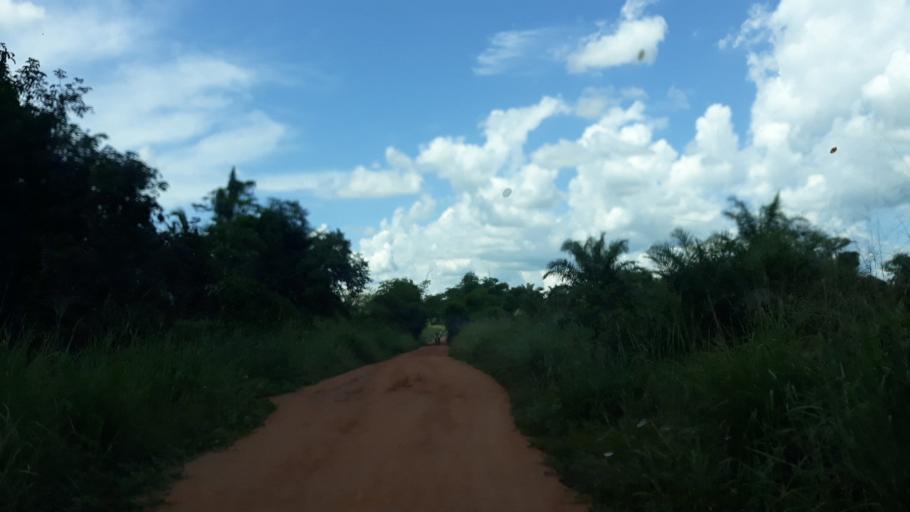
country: CD
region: Equateur
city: Businga
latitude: 3.4035
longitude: 20.3826
